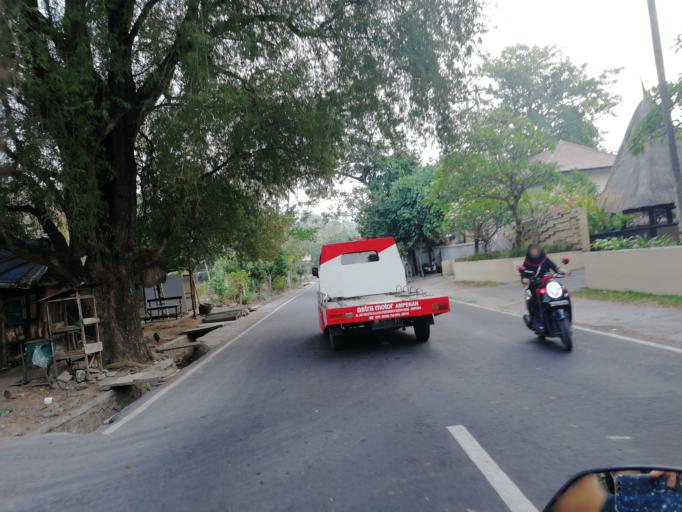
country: ID
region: West Nusa Tenggara
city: Karangsubagan
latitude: -8.4788
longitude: 116.0388
